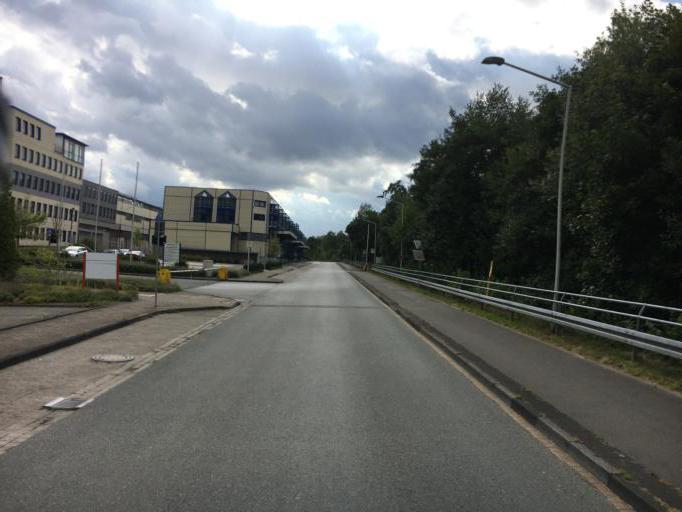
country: DE
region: North Rhine-Westphalia
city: Plettenberg
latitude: 51.1970
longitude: 7.8260
